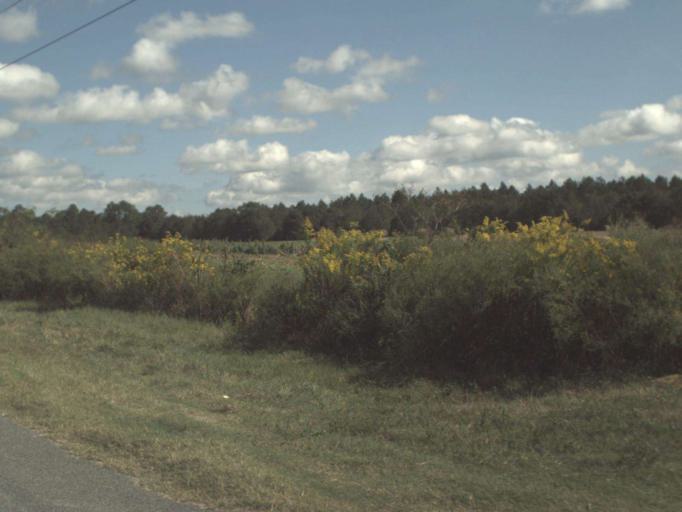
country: US
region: Florida
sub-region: Walton County
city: DeFuniak Springs
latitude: 30.8297
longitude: -86.1204
